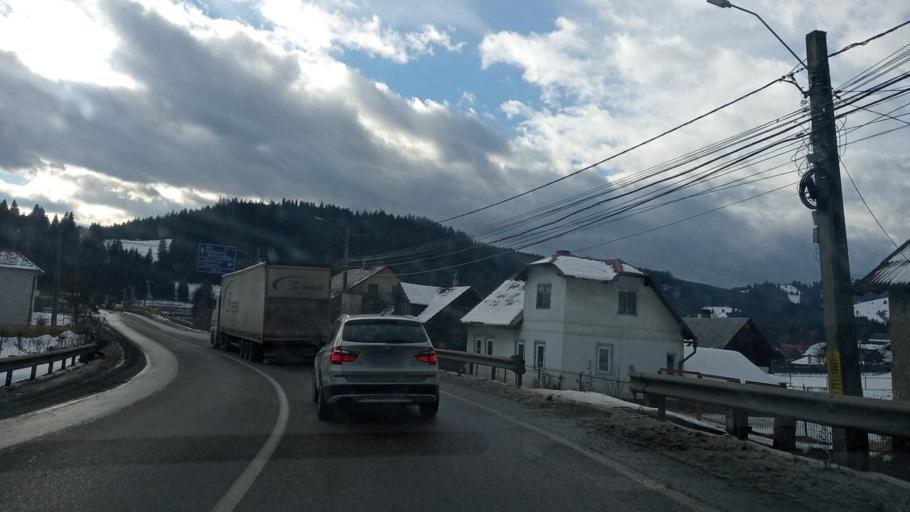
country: RO
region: Suceava
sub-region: Comuna Vama
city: Vama
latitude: 47.5746
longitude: 25.6940
